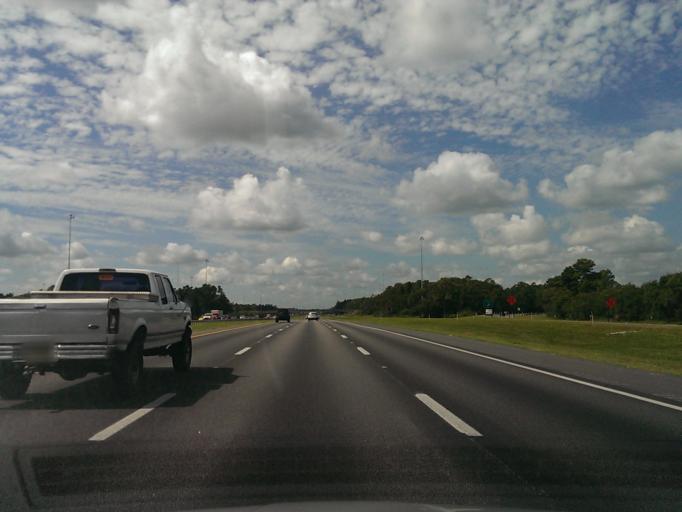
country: US
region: Florida
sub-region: Osceola County
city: Celebration
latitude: 28.3659
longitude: -81.5153
